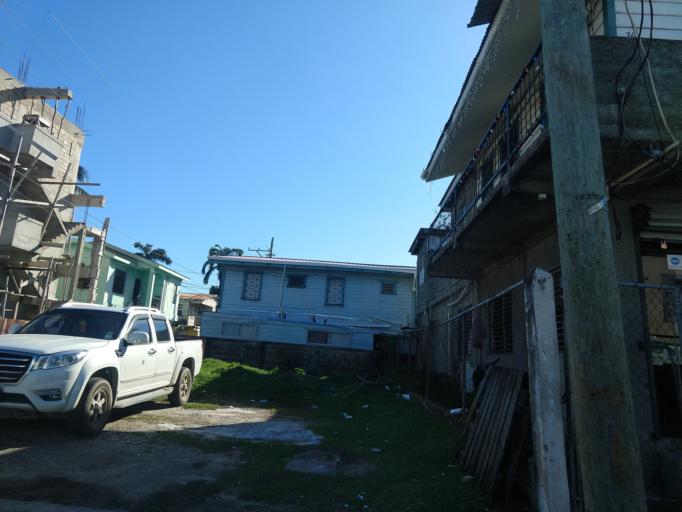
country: BZ
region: Belize
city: Belize City
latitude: 17.5014
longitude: -88.1883
